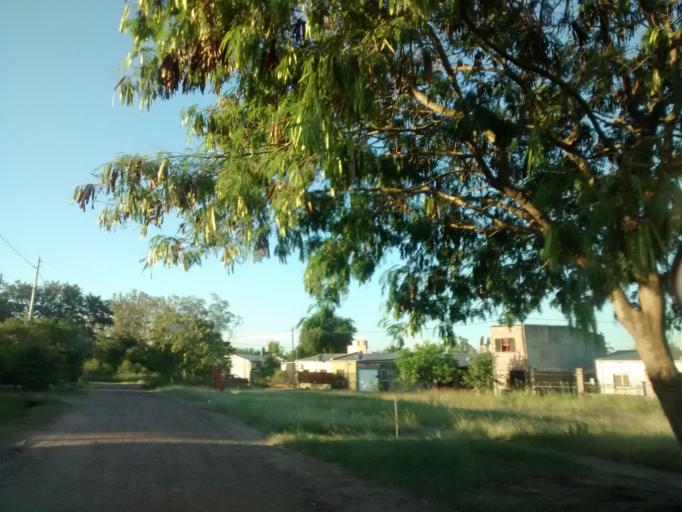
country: AR
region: Chaco
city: Fontana
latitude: -27.4382
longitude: -59.0255
